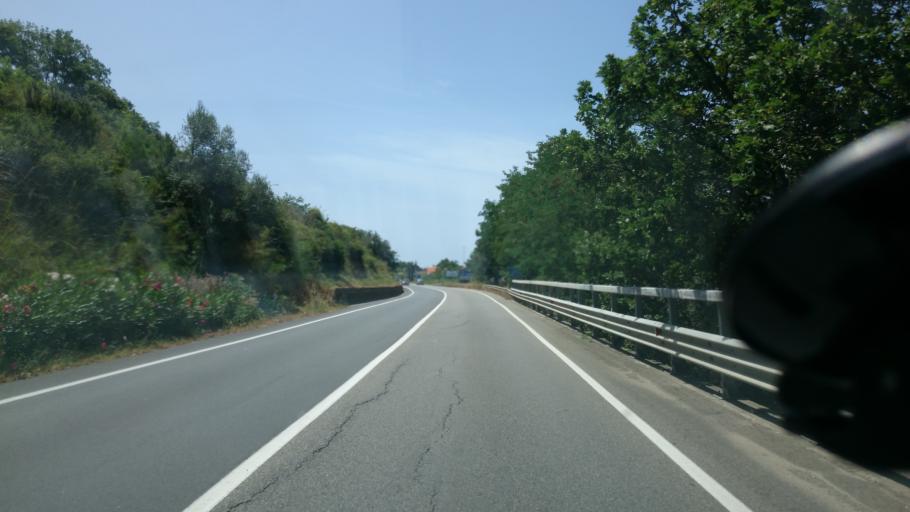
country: IT
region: Calabria
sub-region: Provincia di Cosenza
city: Cittadella del Capo
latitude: 39.5842
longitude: 15.8701
